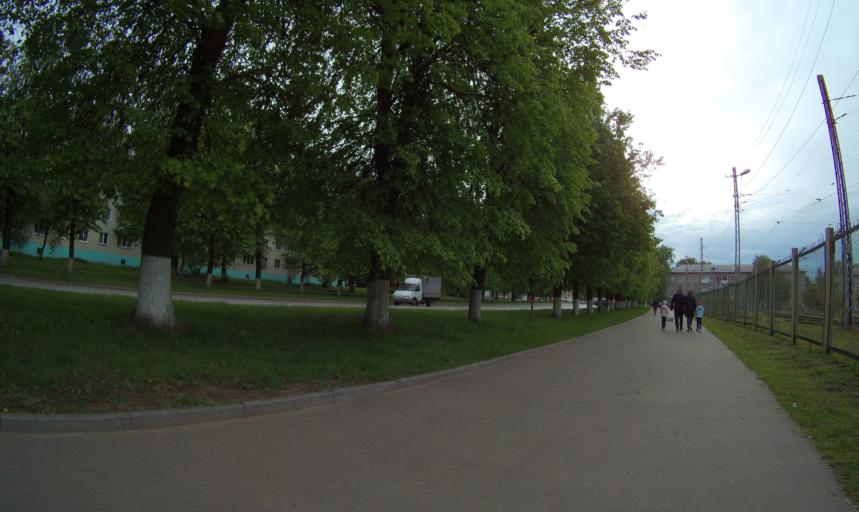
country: RU
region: Moskovskaya
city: Kolomna
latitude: 55.0874
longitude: 38.7676
